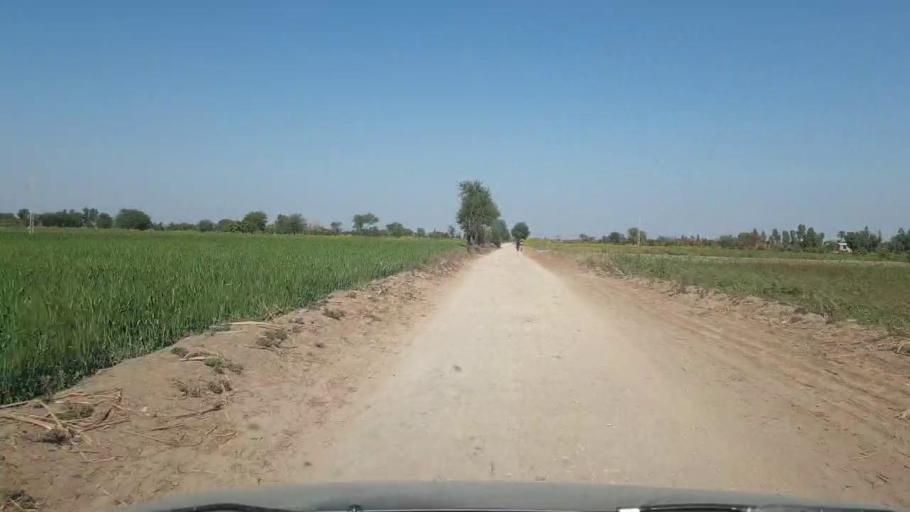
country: PK
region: Sindh
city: Samaro
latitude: 25.3071
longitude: 69.2689
